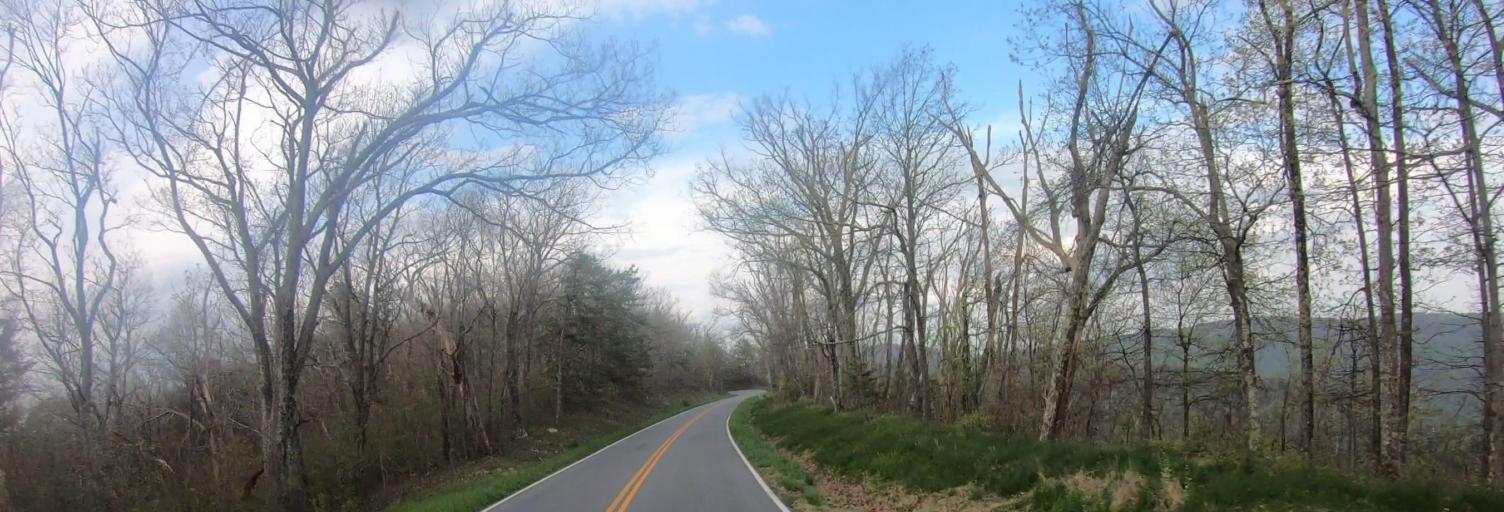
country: US
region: Virginia
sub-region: Augusta County
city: Crimora
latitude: 38.1693
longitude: -78.7693
